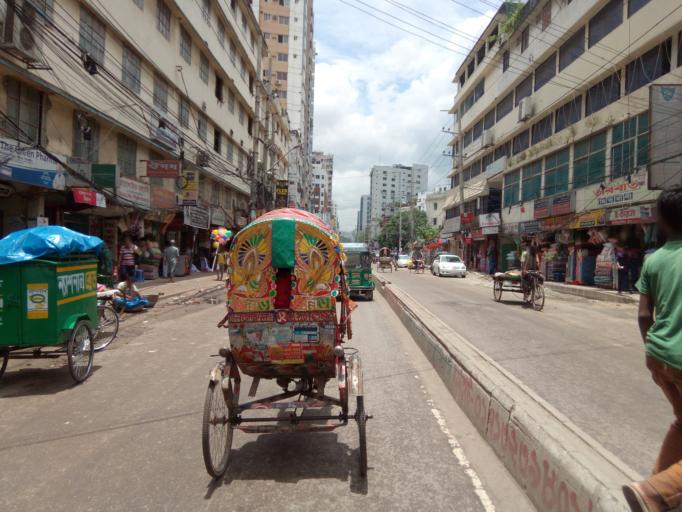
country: BD
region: Dhaka
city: Azimpur
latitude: 23.7476
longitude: 90.3860
